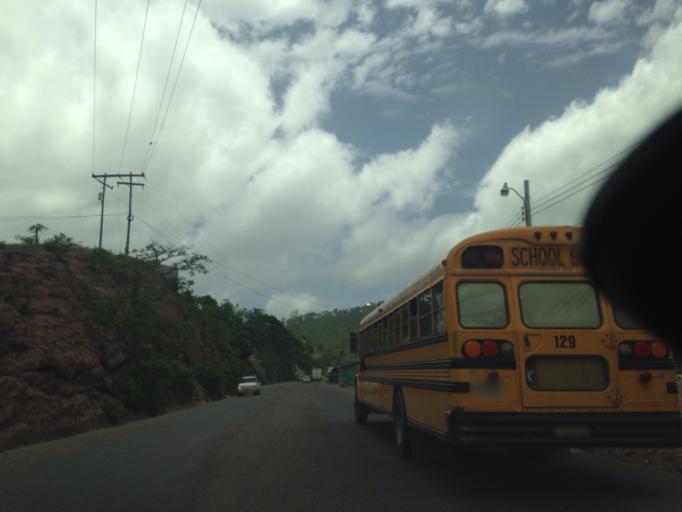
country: HN
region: Francisco Morazan
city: El Tablon
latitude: 14.0530
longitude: -87.1571
